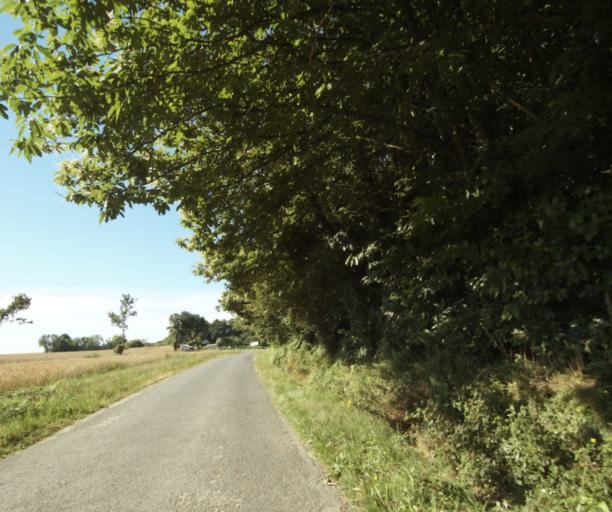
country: FR
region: Pays de la Loire
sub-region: Departement de la Mayenne
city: Laval
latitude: 48.0427
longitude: -0.7527
